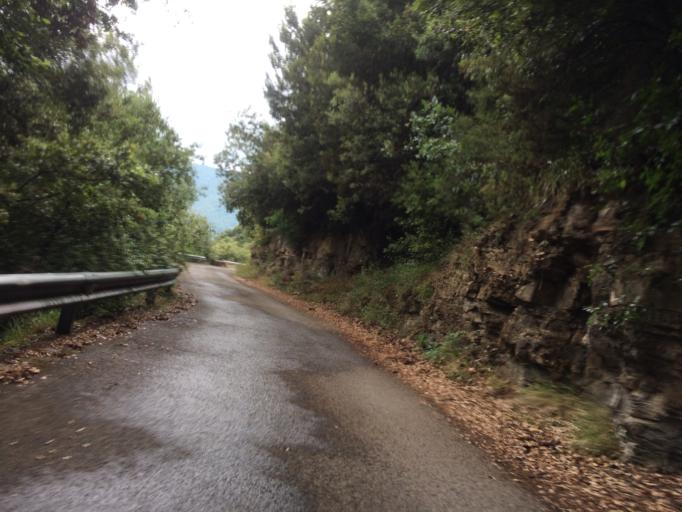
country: IT
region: Liguria
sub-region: Provincia di Imperia
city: Castel Vittorio
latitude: 43.9455
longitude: 7.6968
